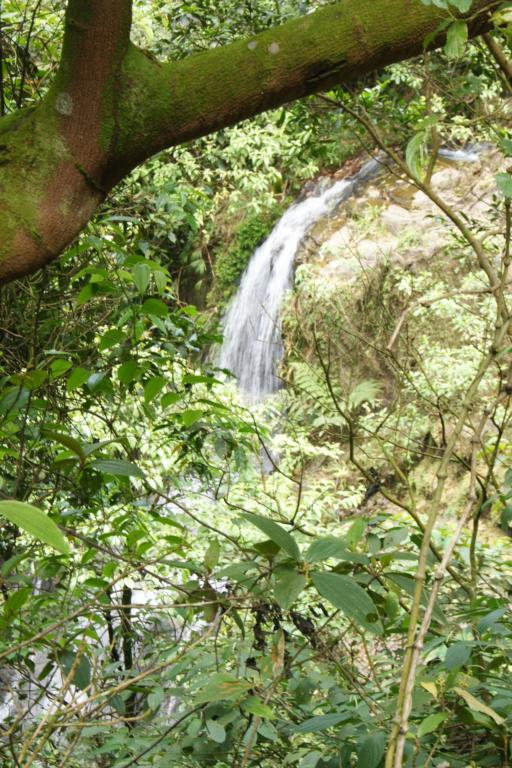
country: BR
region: Sao Paulo
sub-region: Cubatao
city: Cubatao
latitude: -23.8582
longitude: -46.4465
